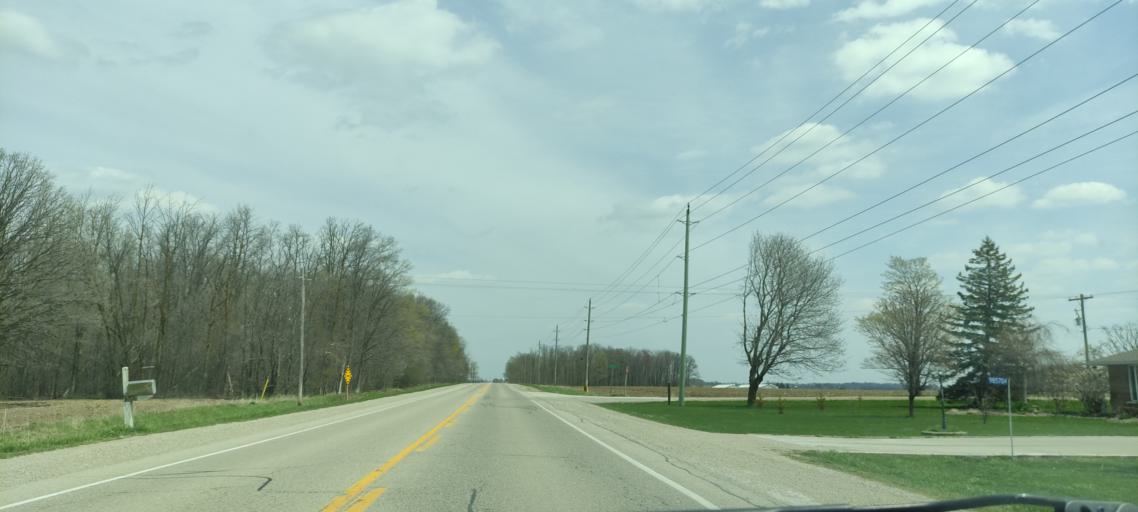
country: CA
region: Ontario
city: Stratford
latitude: 43.3396
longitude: -80.7778
